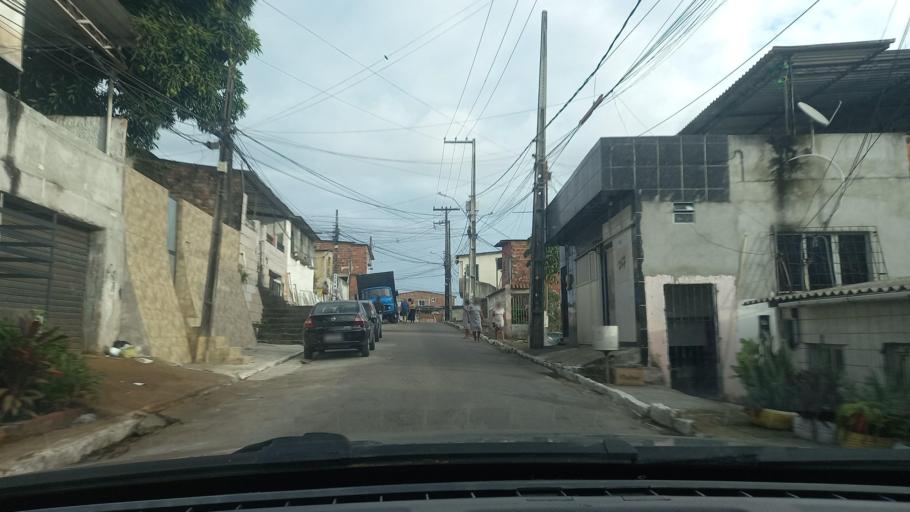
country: BR
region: Pernambuco
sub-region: Jaboatao Dos Guararapes
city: Jaboatao dos Guararapes
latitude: -8.1243
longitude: -34.9474
